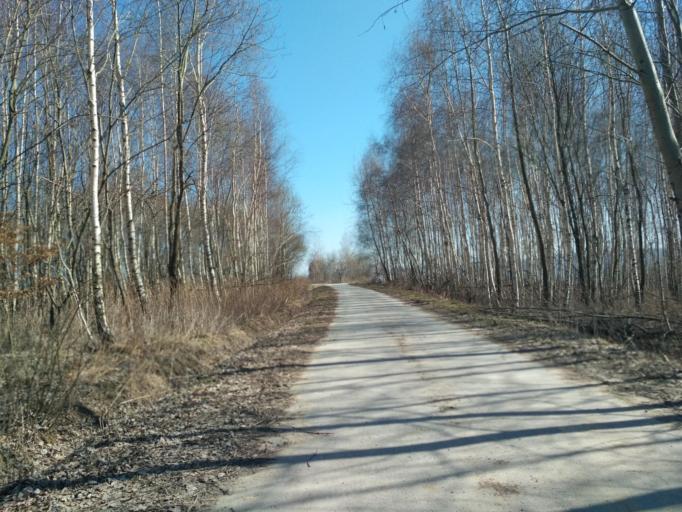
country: PL
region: Subcarpathian Voivodeship
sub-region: Powiat ropczycko-sedziszowski
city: Niedzwiada
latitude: 49.9554
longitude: 21.5532
